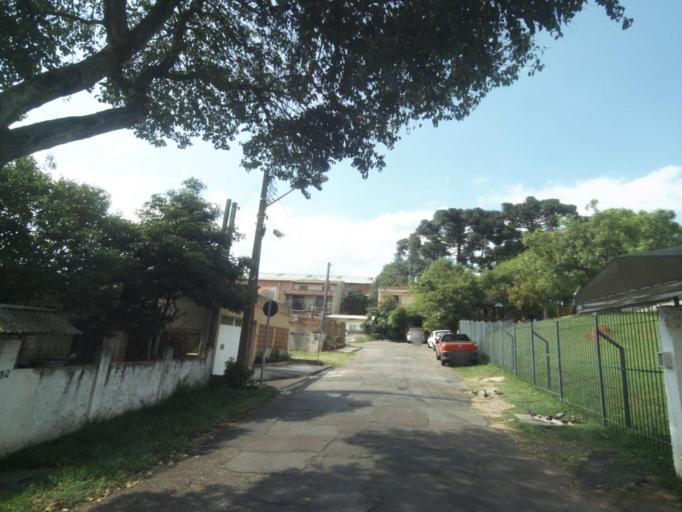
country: BR
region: Parana
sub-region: Curitiba
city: Curitiba
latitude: -25.4988
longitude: -49.3149
